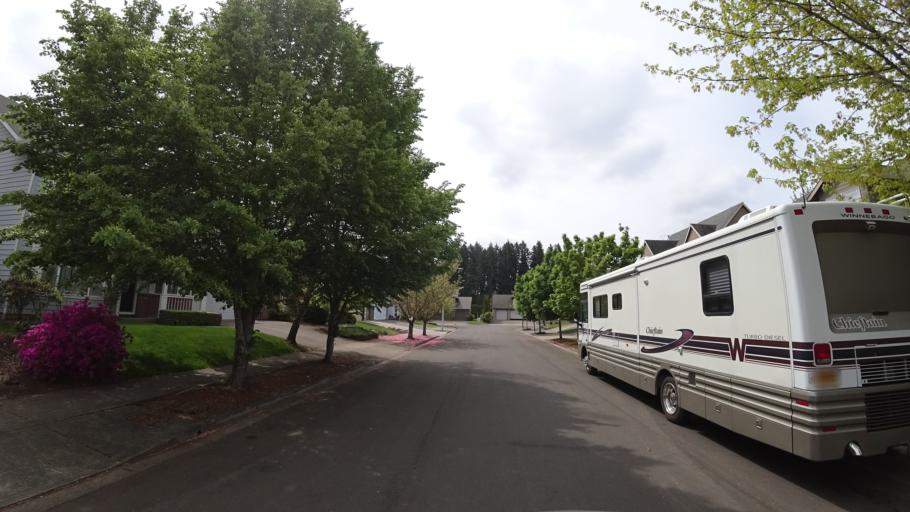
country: US
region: Oregon
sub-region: Washington County
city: Hillsboro
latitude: 45.5446
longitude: -122.9911
